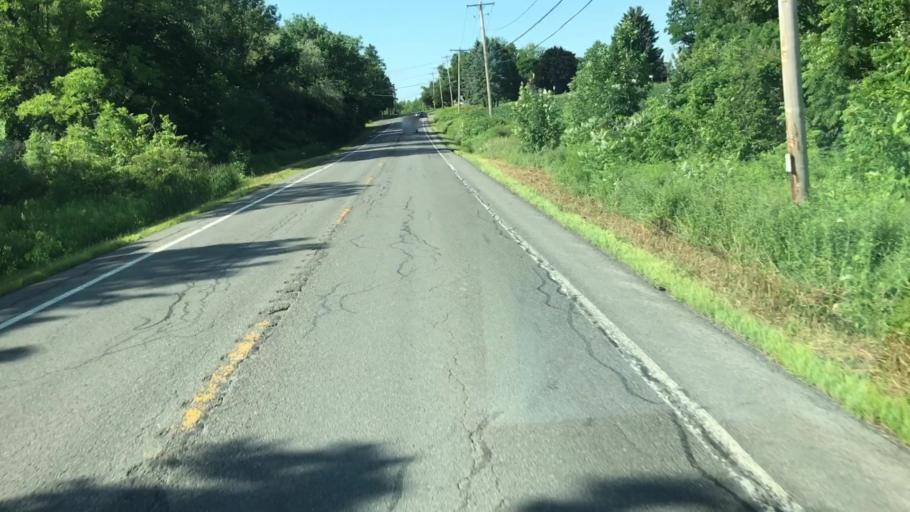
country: US
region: New York
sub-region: Onondaga County
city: Elbridge
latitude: 42.9948
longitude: -76.4272
